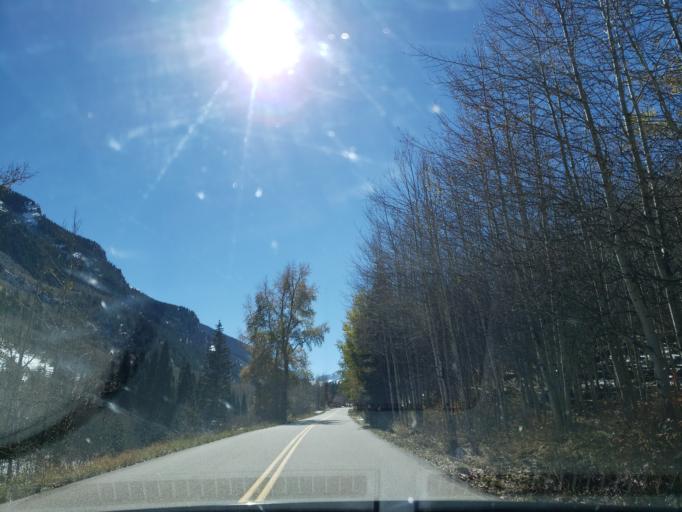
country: US
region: Colorado
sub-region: Pitkin County
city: Snowmass Village
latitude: 39.1385
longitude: -106.8986
